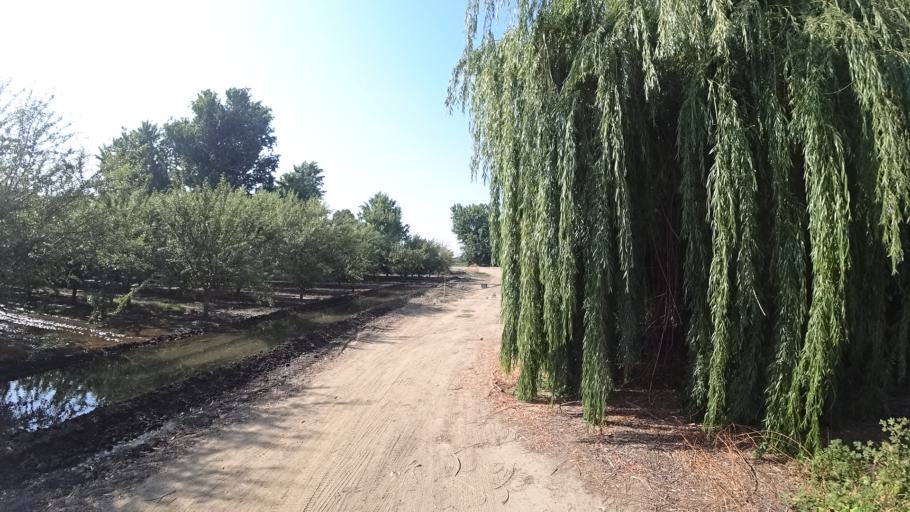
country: US
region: California
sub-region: Kings County
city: Lemoore
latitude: 36.3506
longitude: -119.8430
